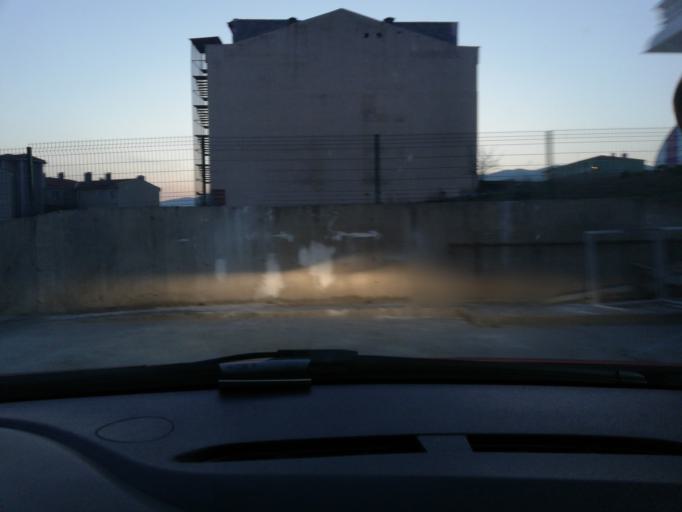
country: TR
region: Karabuk
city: Safranbolu
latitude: 41.2195
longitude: 32.6705
